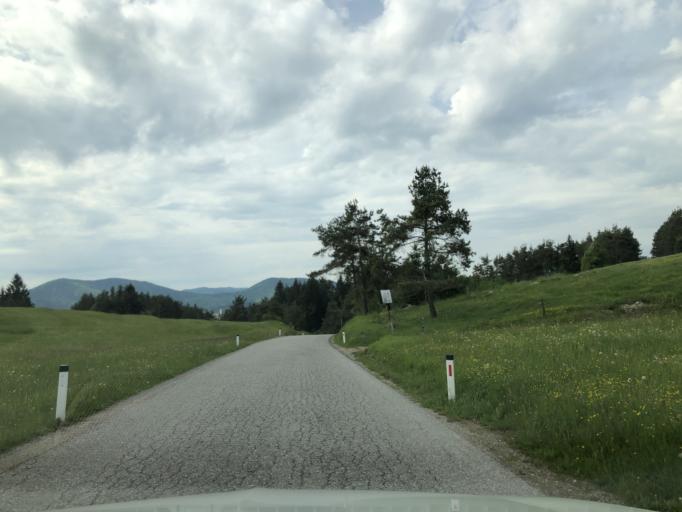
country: SI
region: Bloke
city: Nova Vas
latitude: 45.7831
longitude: 14.5010
